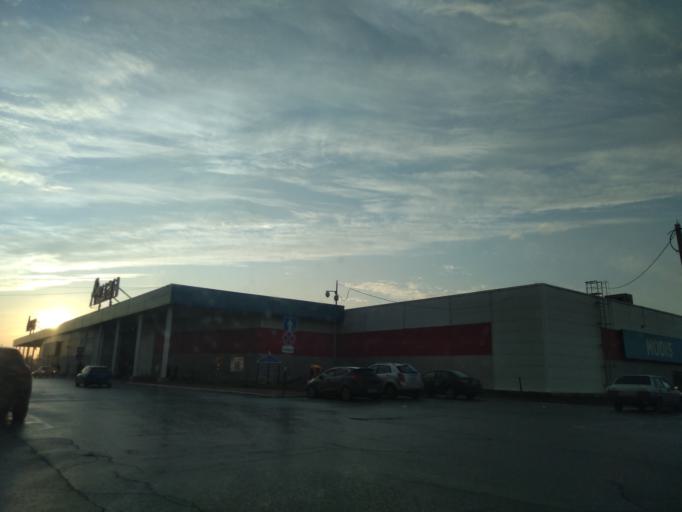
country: RU
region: Lipetsk
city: Syrskoye
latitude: 52.5745
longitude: 39.5248
